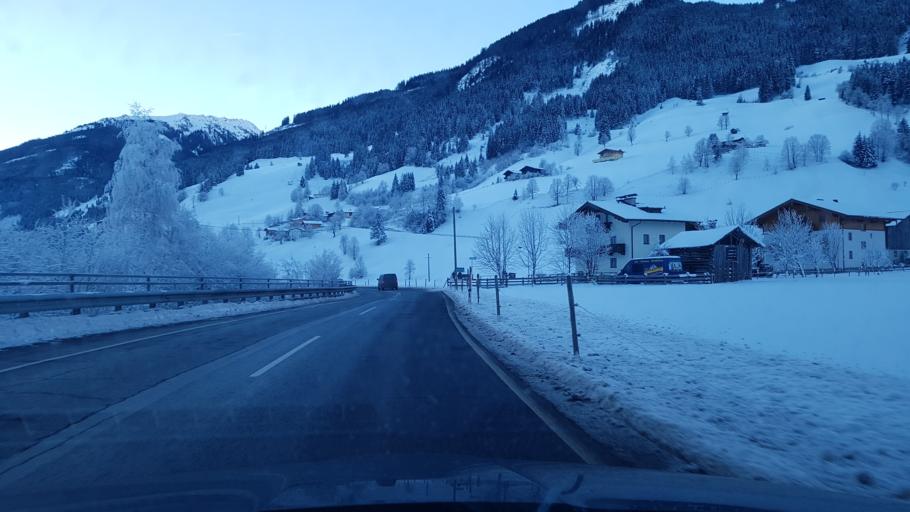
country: AT
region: Salzburg
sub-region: Politischer Bezirk Sankt Johann im Pongau
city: Huttschlag
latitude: 47.2118
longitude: 13.1994
